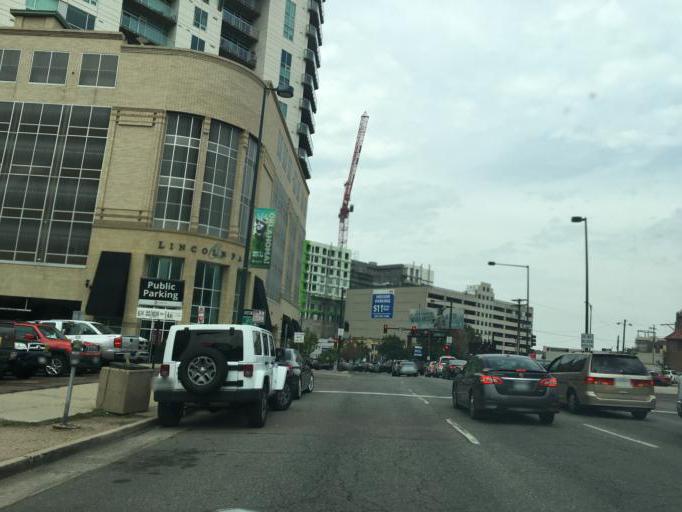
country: US
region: Colorado
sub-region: Denver County
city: Denver
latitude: 39.7472
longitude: -104.9862
